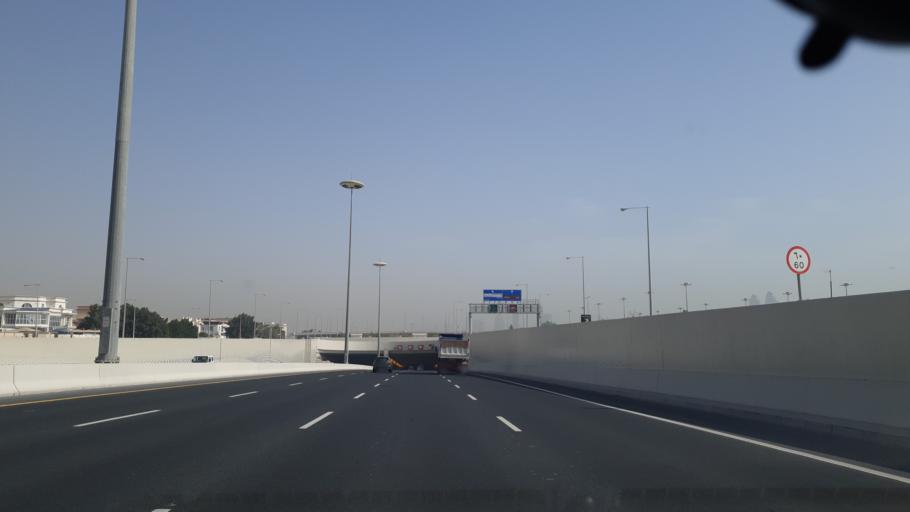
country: QA
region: Baladiyat ad Dawhah
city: Doha
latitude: 25.3473
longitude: 51.5204
